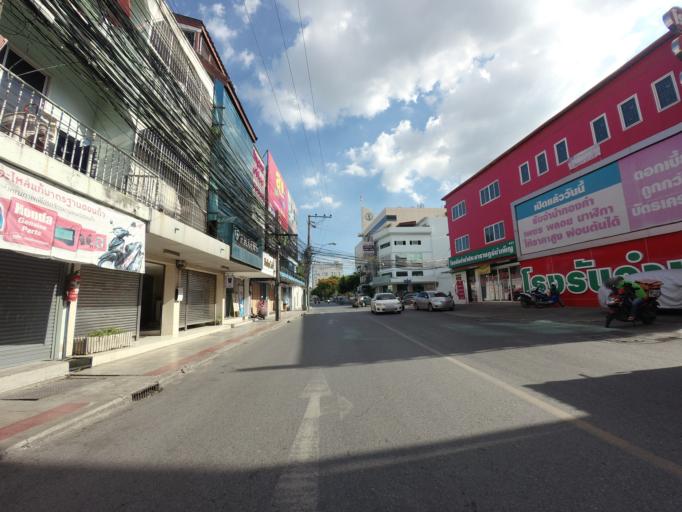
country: TH
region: Bangkok
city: Huai Khwang
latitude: 13.7775
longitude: 100.5801
